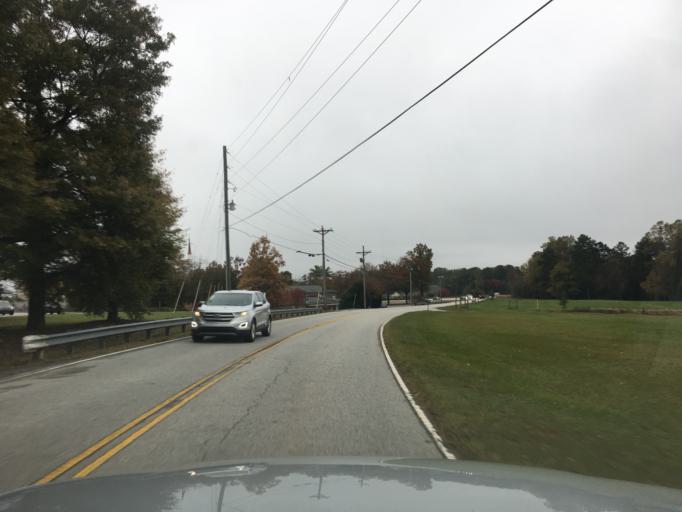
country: US
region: South Carolina
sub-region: Greenville County
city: Five Forks
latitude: 34.8404
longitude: -82.2705
